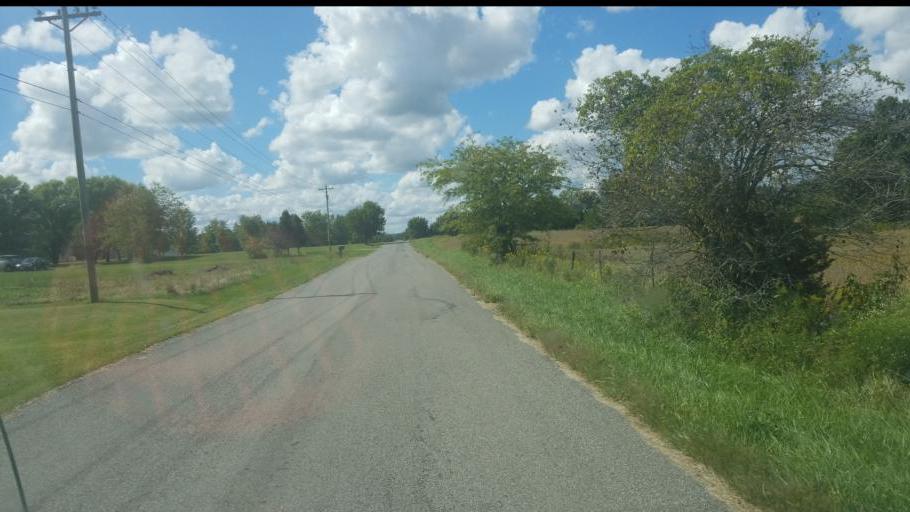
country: US
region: Ohio
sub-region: Champaign County
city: North Lewisburg
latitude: 40.3308
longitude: -83.5023
